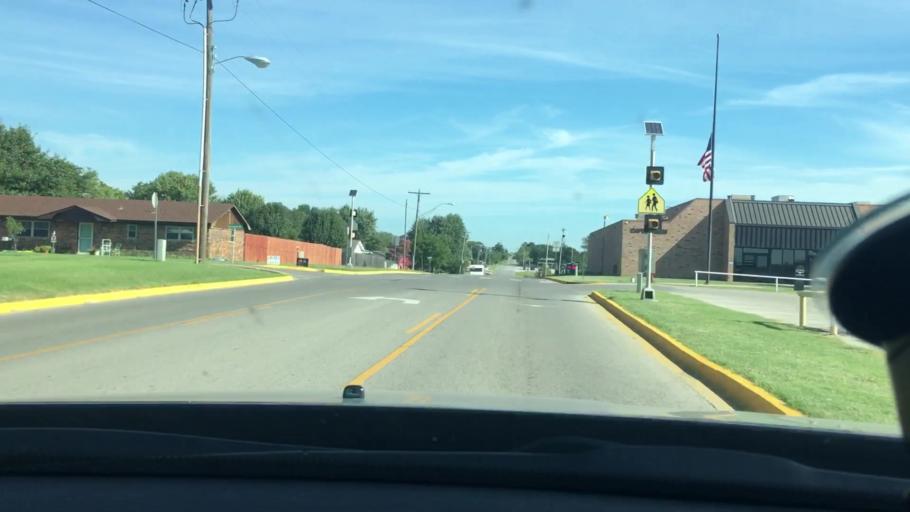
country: US
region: Oklahoma
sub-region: Carter County
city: Lone Grove
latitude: 34.1775
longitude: -97.2474
